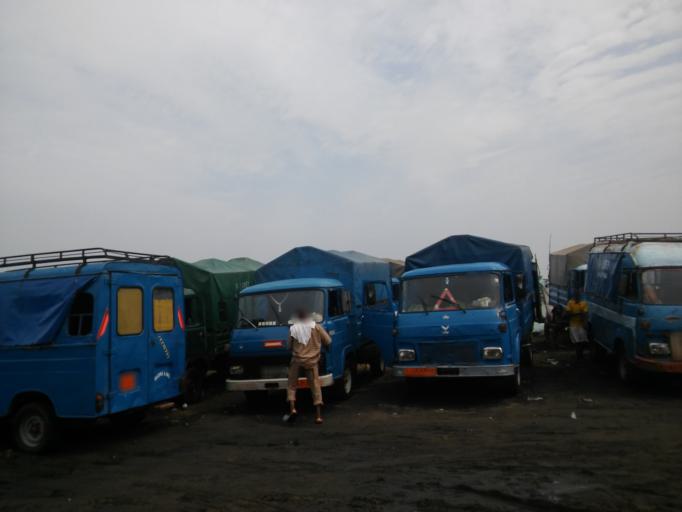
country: BJ
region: Littoral
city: Cotonou
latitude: 6.3648
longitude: 2.4376
